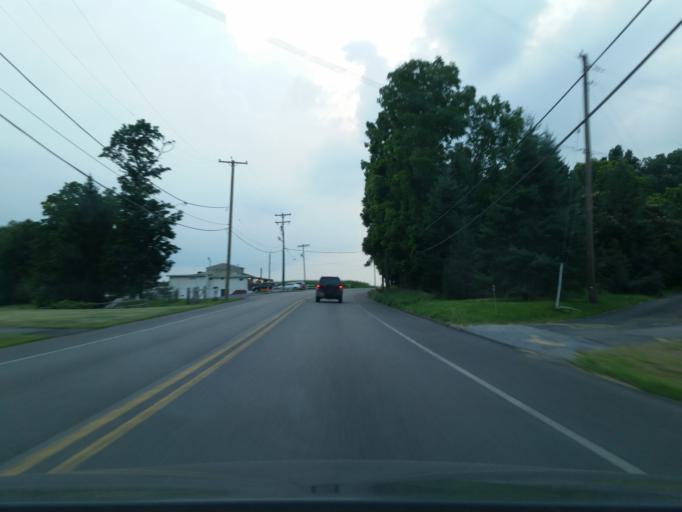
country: US
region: Pennsylvania
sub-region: Lebanon County
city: Jonestown
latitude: 40.3967
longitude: -76.4885
